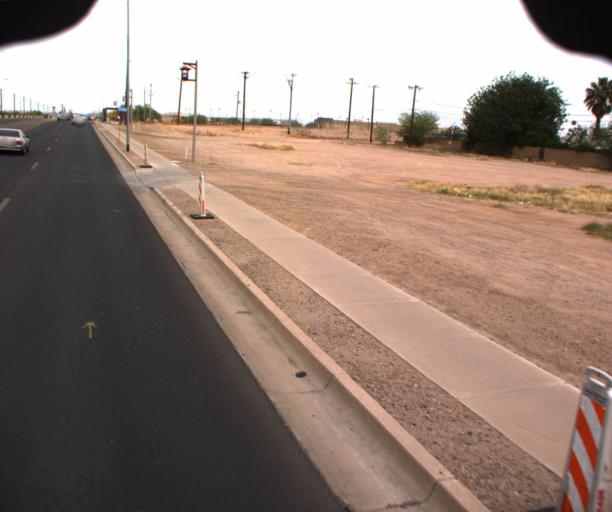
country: US
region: Arizona
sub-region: Pinal County
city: Coolidge
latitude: 32.9903
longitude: -111.5239
